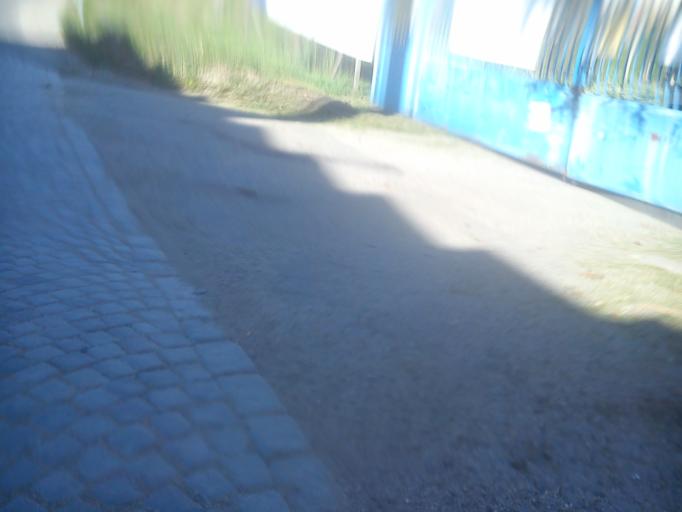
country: CZ
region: South Moravian
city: Sokolnice
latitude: 49.1073
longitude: 16.7374
